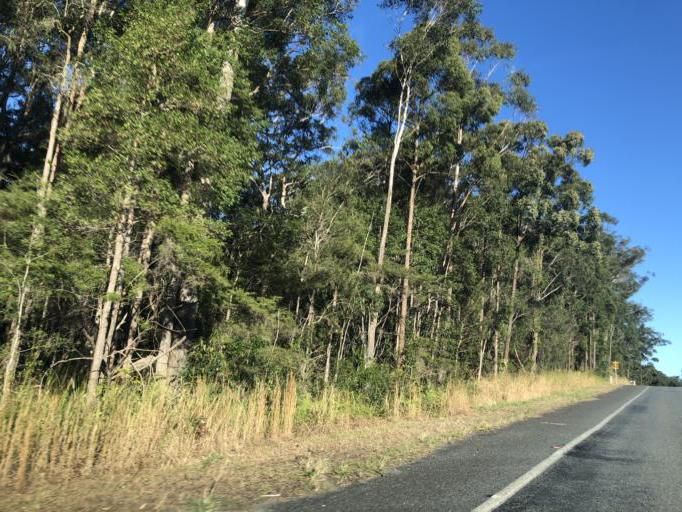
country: AU
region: New South Wales
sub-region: Nambucca Shire
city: Nambucca
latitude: -30.5587
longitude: 153.0051
